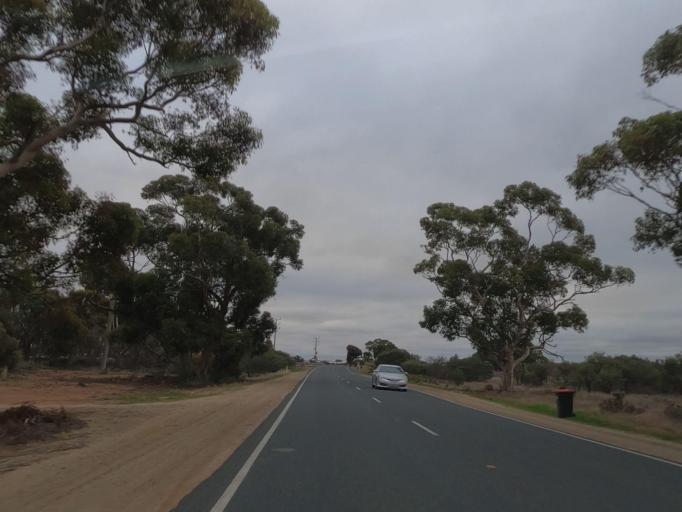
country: AU
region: Victoria
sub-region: Swan Hill
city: Swan Hill
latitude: -35.3966
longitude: 143.5738
